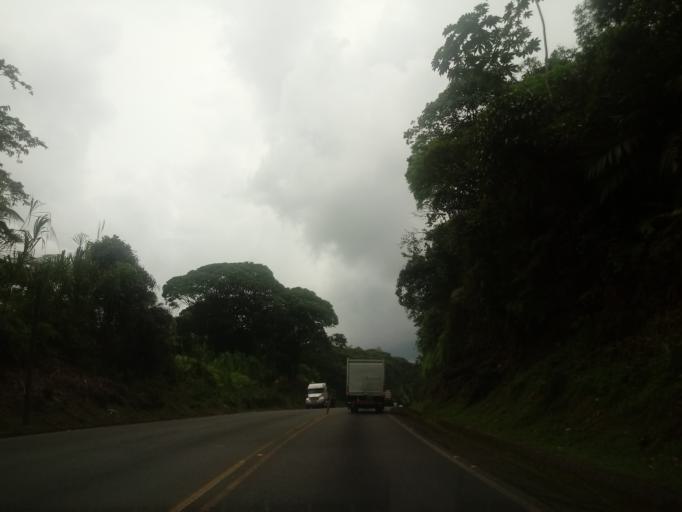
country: CR
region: San Jose
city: Dulce Nombre de Jesus
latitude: 10.1737
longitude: -83.9319
